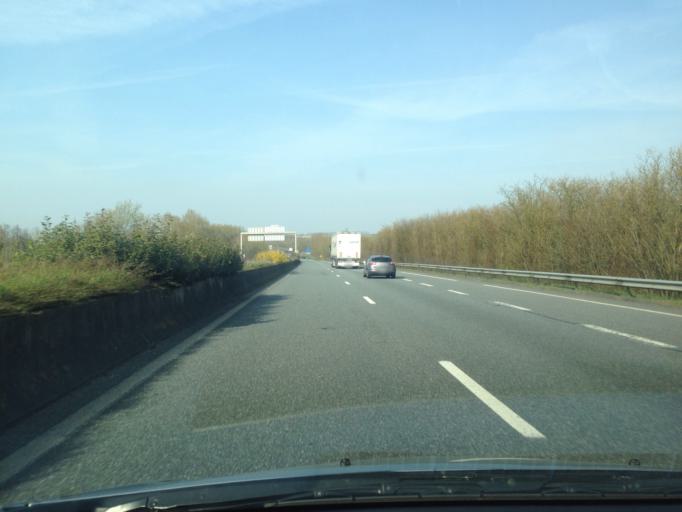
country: FR
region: Picardie
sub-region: Departement de la Somme
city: Abbeville
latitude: 50.1088
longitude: 1.7888
